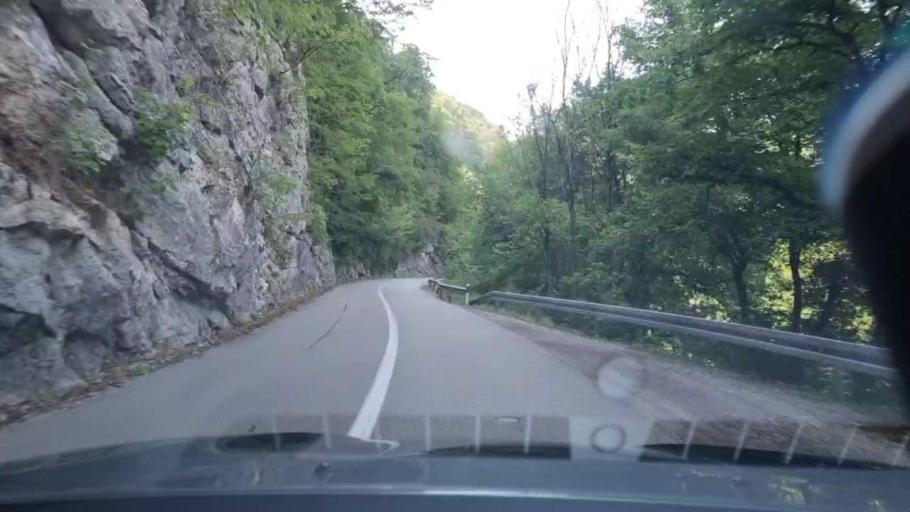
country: BA
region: Federation of Bosnia and Herzegovina
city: Bosanska Krupa
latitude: 44.8655
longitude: 16.0905
